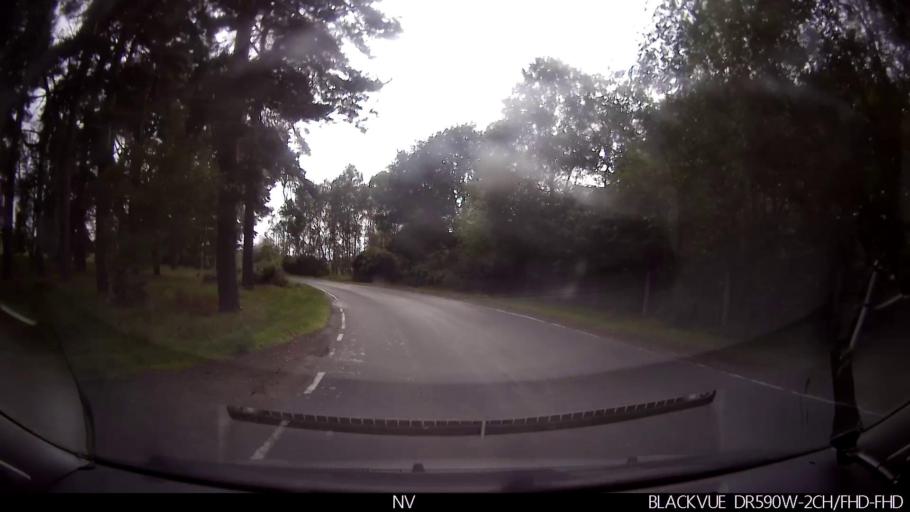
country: GB
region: England
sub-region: North Yorkshire
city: Strensall
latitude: 54.0480
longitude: -1.0047
